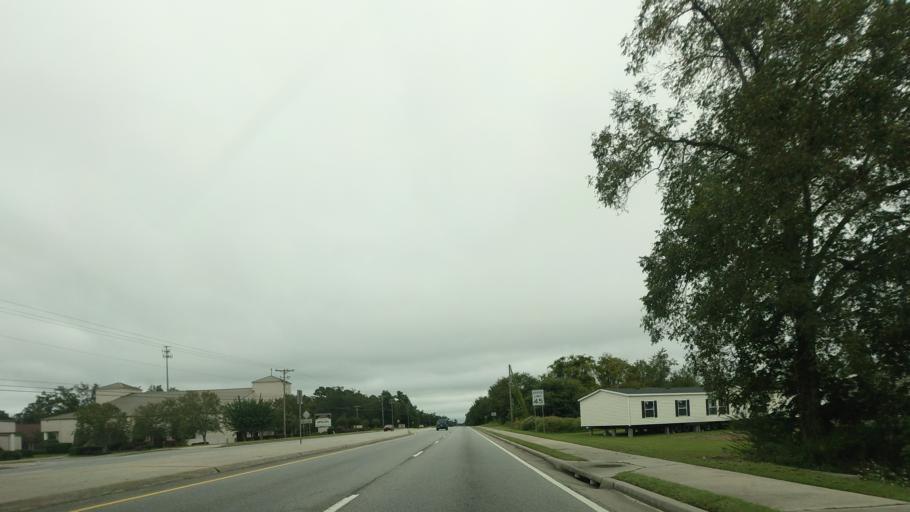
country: US
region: Georgia
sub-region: Lowndes County
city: Valdosta
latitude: 30.8910
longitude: -83.2703
